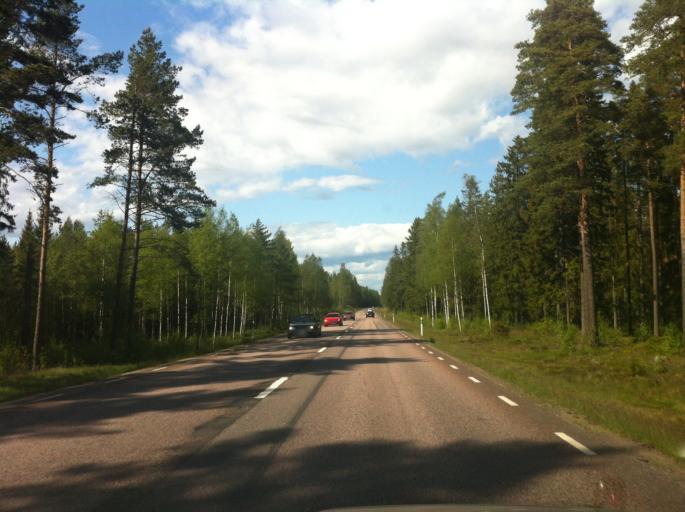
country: SE
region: Vaermland
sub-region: Kristinehamns Kommun
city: Bjorneborg
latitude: 59.1997
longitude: 14.1831
